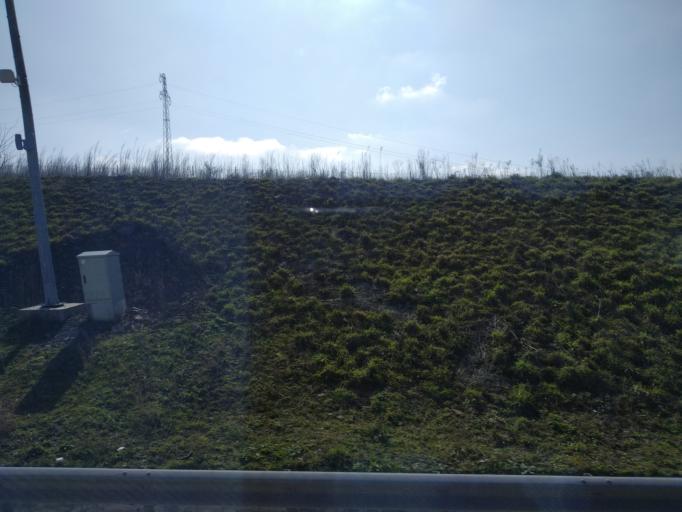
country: TR
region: Istanbul
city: Kemerburgaz
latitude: 41.2304
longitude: 28.8505
